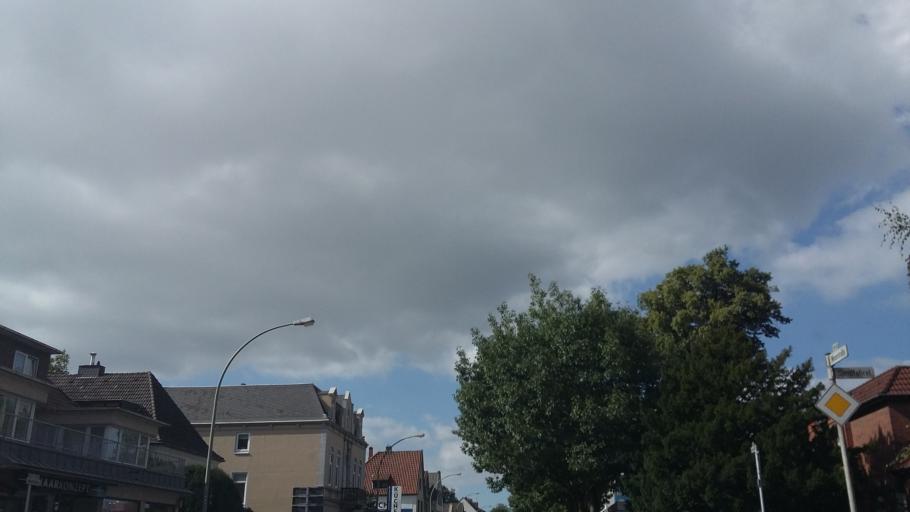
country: DE
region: Bremen
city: Bremerhaven
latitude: 53.5070
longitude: 8.5979
